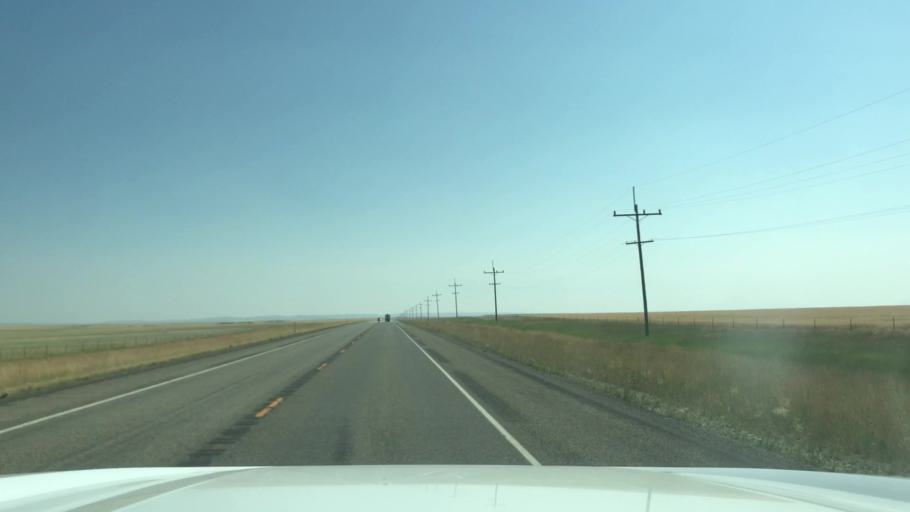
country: US
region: Montana
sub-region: Wheatland County
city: Harlowton
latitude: 46.5120
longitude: -109.7660
